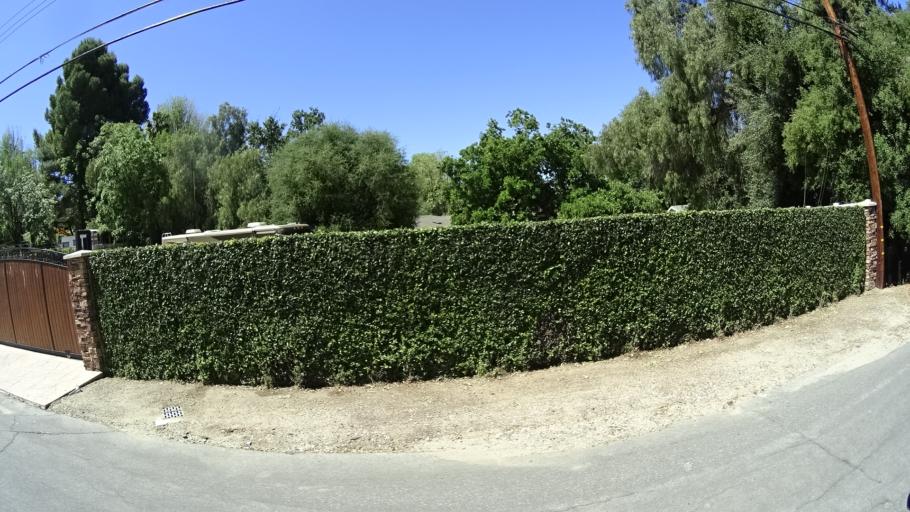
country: US
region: California
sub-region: Ventura County
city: Thousand Oaks
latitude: 34.1838
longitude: -118.8579
